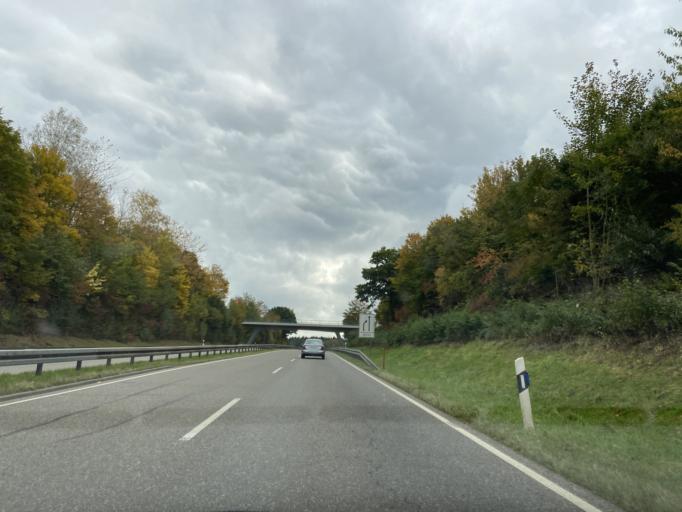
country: DE
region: Baden-Wuerttemberg
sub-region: Tuebingen Region
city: Sigmaringen
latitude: 48.0714
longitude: 9.2148
